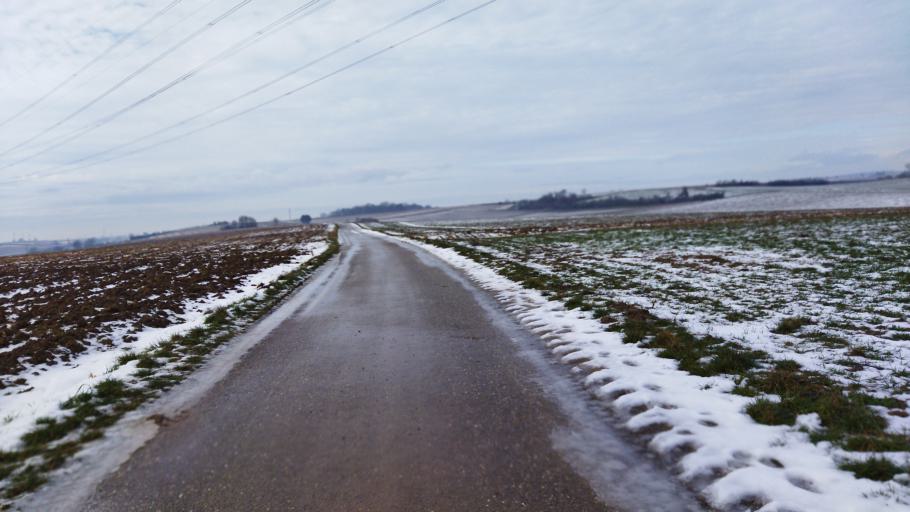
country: DE
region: Baden-Wuerttemberg
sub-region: Regierungsbezirk Stuttgart
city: Untereisesheim
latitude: 49.1948
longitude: 9.1722
